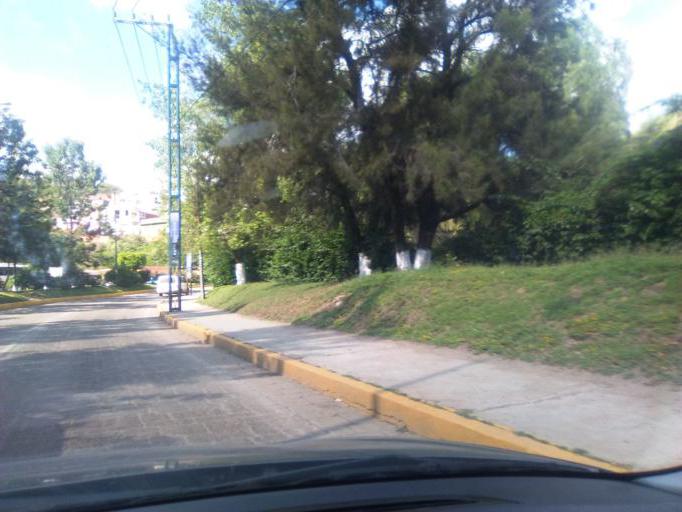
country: MX
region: Guanajuato
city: Guanajuato
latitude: 21.0126
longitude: -101.2674
